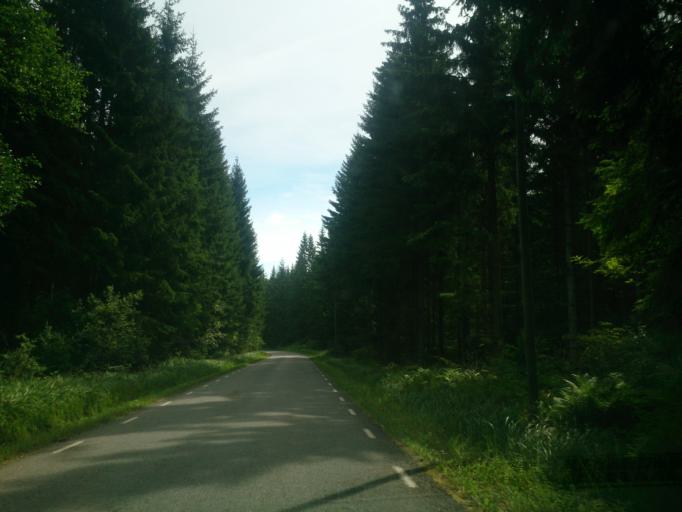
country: SE
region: OEstergoetland
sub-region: Atvidabergs Kommun
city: Atvidaberg
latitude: 58.2761
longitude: 16.1307
